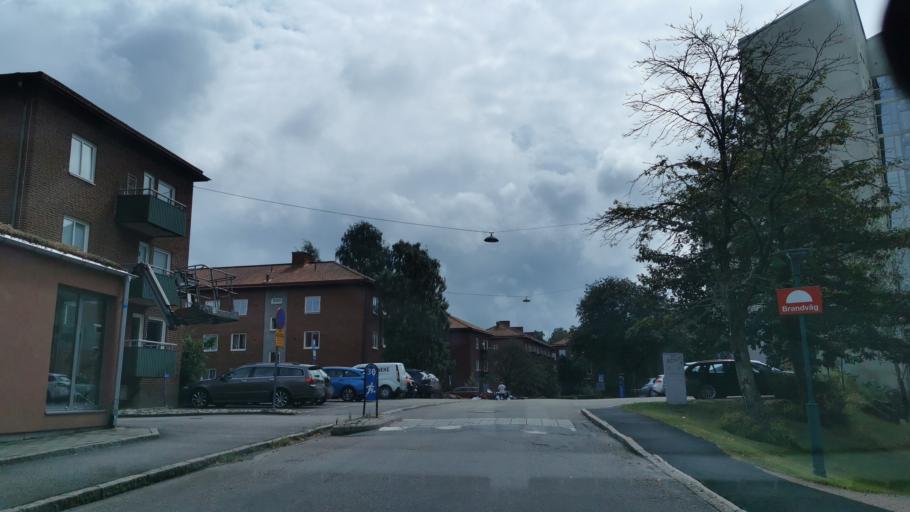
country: SE
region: Vaestra Goetaland
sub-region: Goteborg
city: Goeteborg
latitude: 57.6829
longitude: 11.9770
